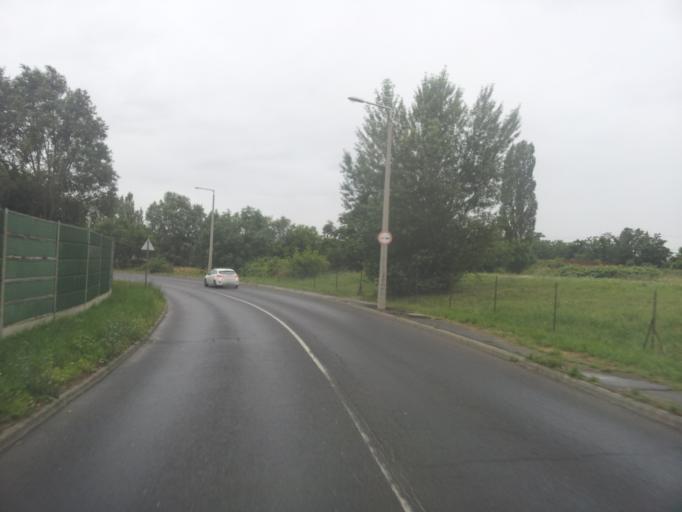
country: HU
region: Budapest
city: Budapest XI. keruelet
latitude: 47.4578
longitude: 19.0232
